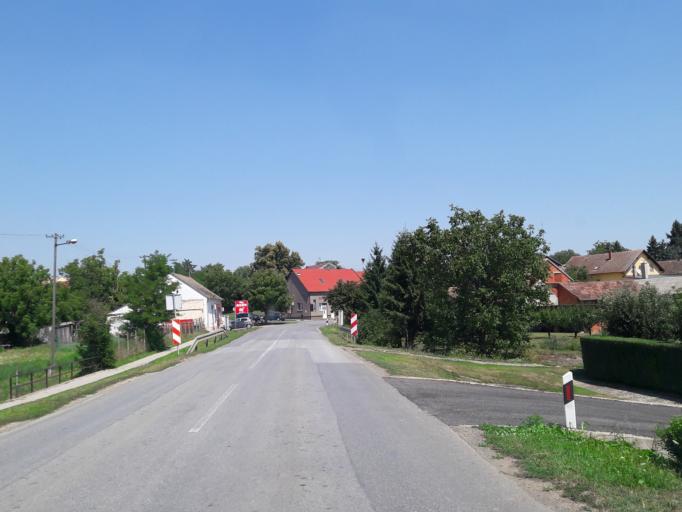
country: HR
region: Osjecko-Baranjska
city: Viskovci
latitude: 45.3446
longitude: 18.4575
